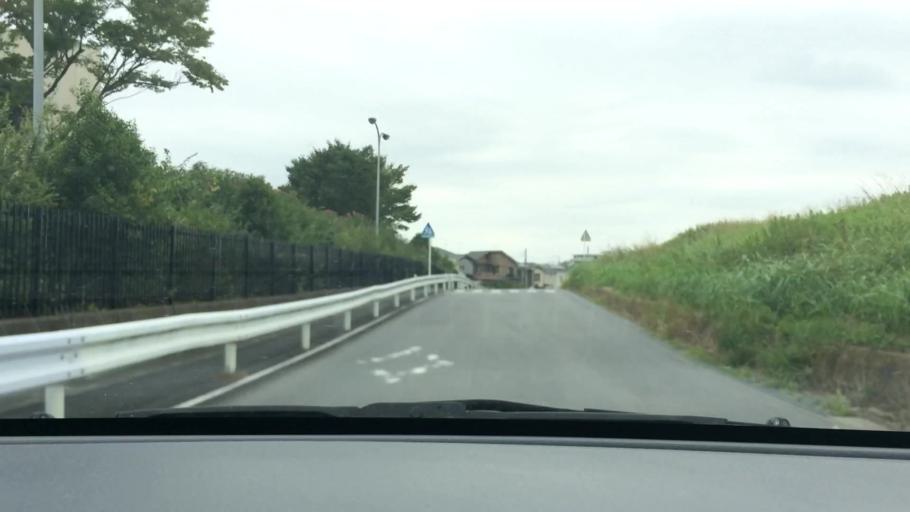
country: JP
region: Chiba
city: Matsudo
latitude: 35.8048
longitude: 139.8861
